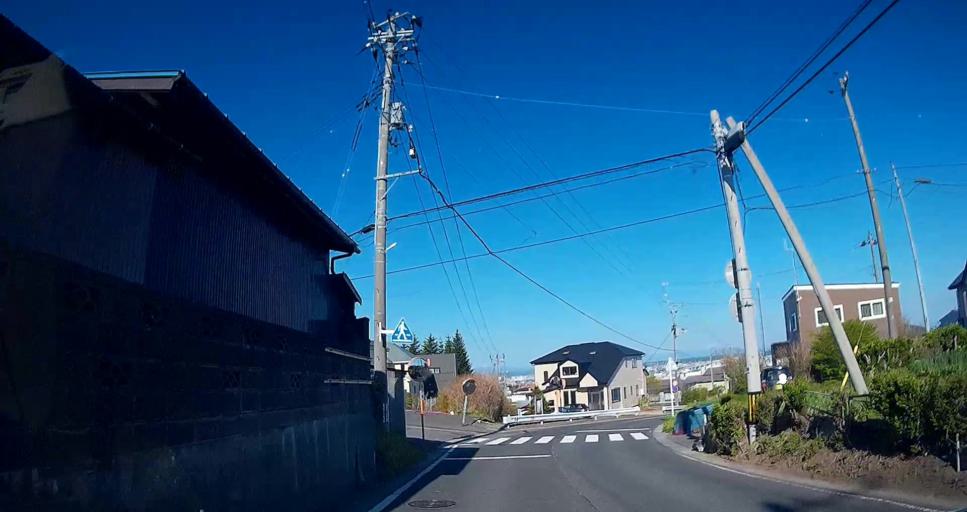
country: JP
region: Aomori
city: Hachinohe
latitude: 40.5224
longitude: 141.5597
